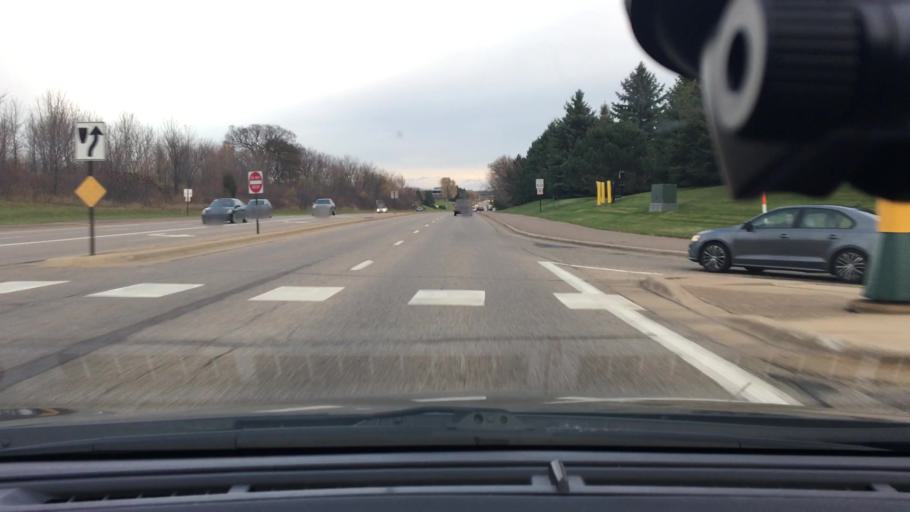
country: US
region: Minnesota
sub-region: Hennepin County
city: Maple Grove
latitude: 45.0584
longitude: -93.4205
